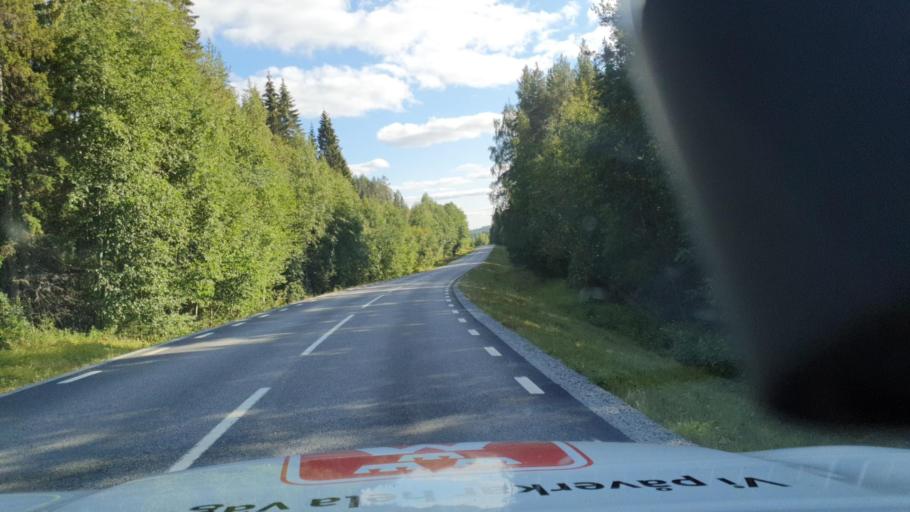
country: SE
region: Vaesterbotten
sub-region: Dorotea Kommun
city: Dorotea
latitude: 63.8649
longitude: 16.3848
